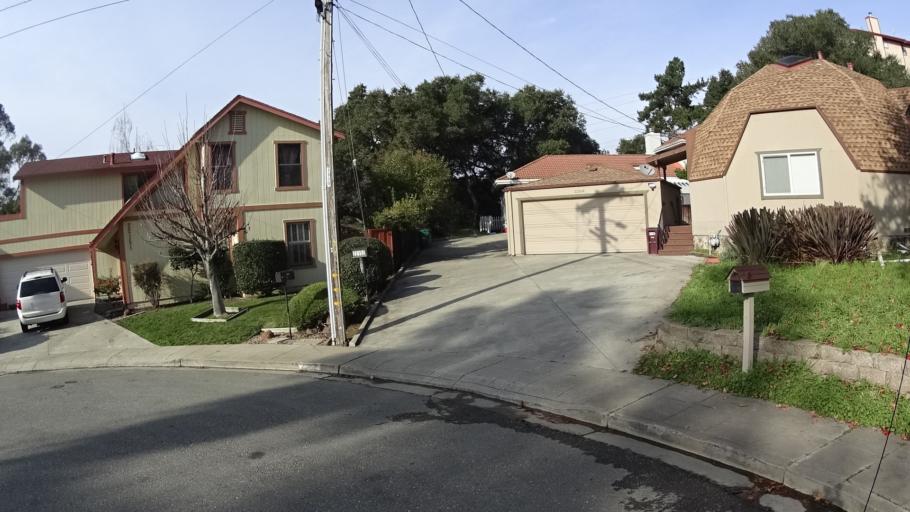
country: US
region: California
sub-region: Alameda County
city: Fairview
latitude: 37.6905
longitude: -122.0586
